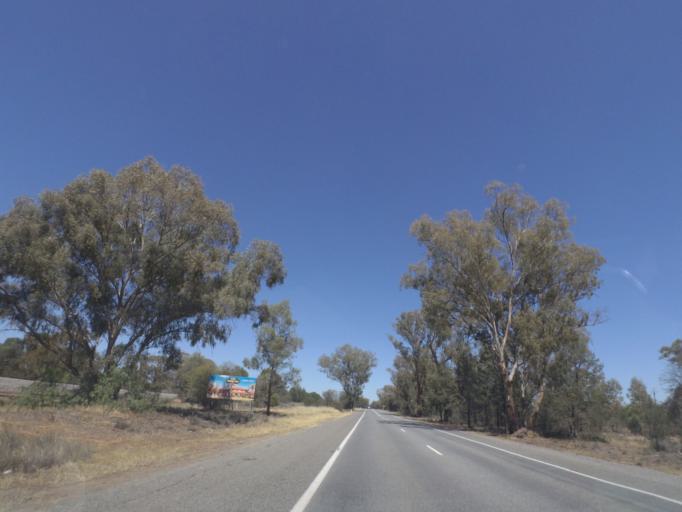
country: AU
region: New South Wales
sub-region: Narrandera
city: Narrandera
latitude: -34.7377
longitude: 146.5836
